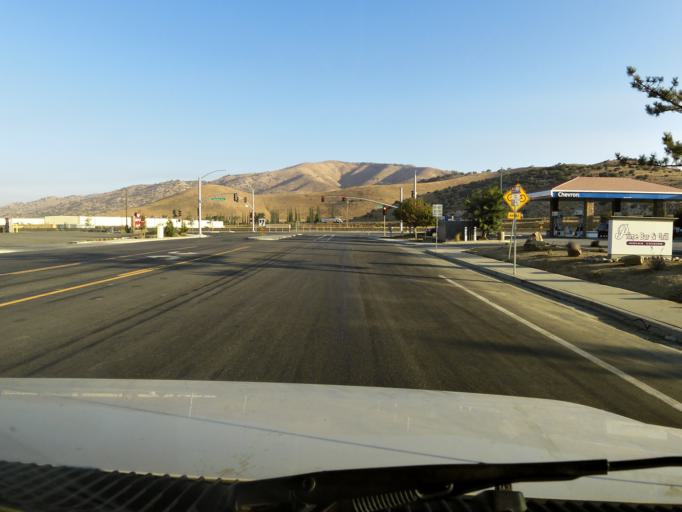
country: US
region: California
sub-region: Kern County
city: Tehachapi
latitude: 35.1268
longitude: -118.4142
